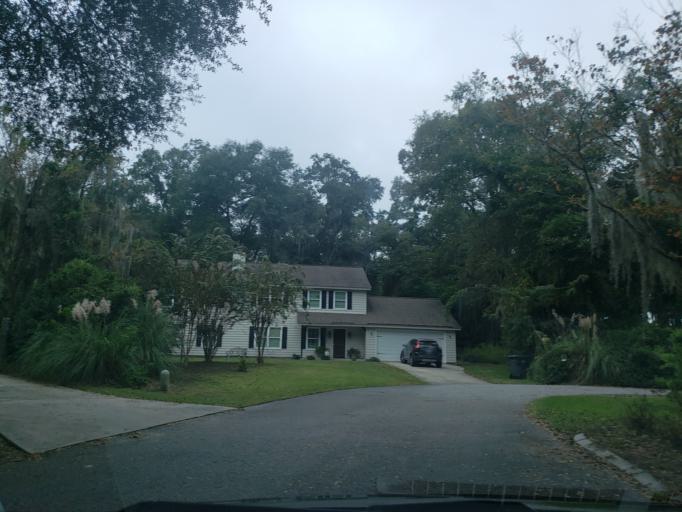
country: US
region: Georgia
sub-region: Chatham County
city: Montgomery
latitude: 31.9545
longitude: -81.1120
